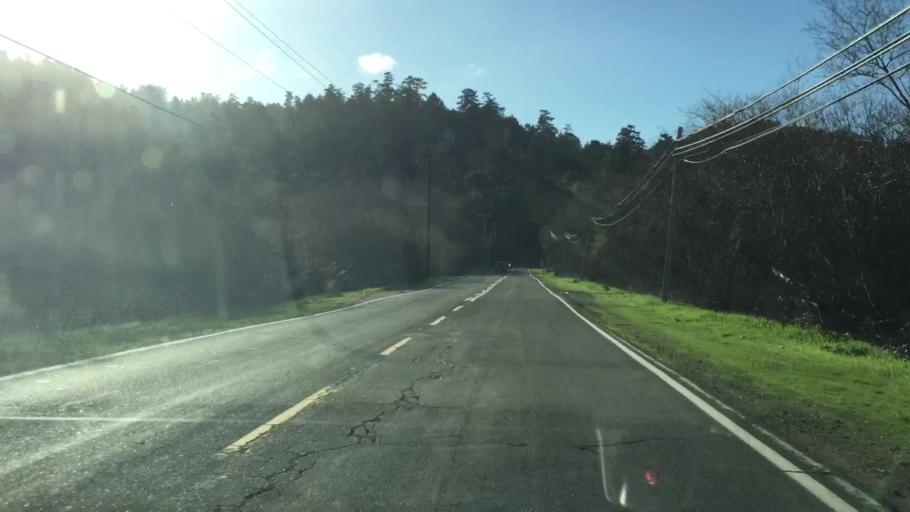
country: US
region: California
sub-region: Marin County
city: Inverness
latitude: 38.0624
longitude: -122.8146
